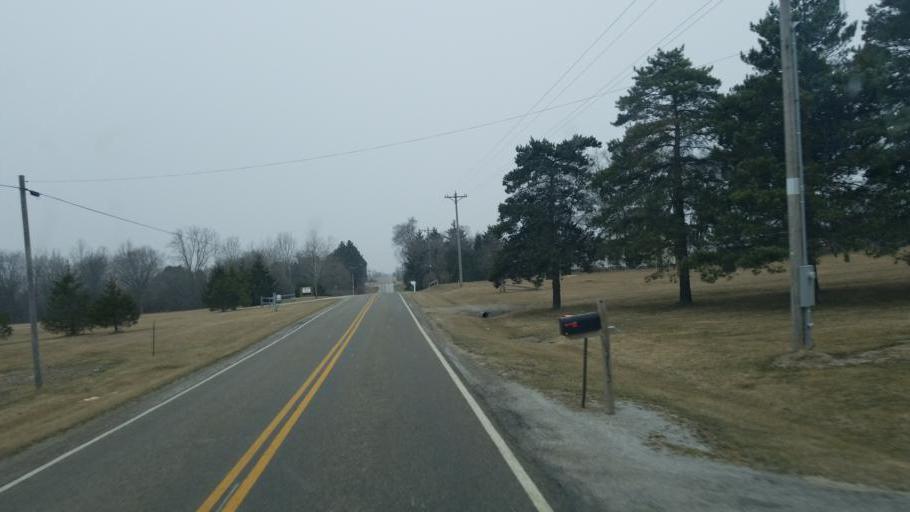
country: US
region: Ohio
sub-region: Defiance County
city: Hicksville
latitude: 41.3249
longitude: -84.7521
